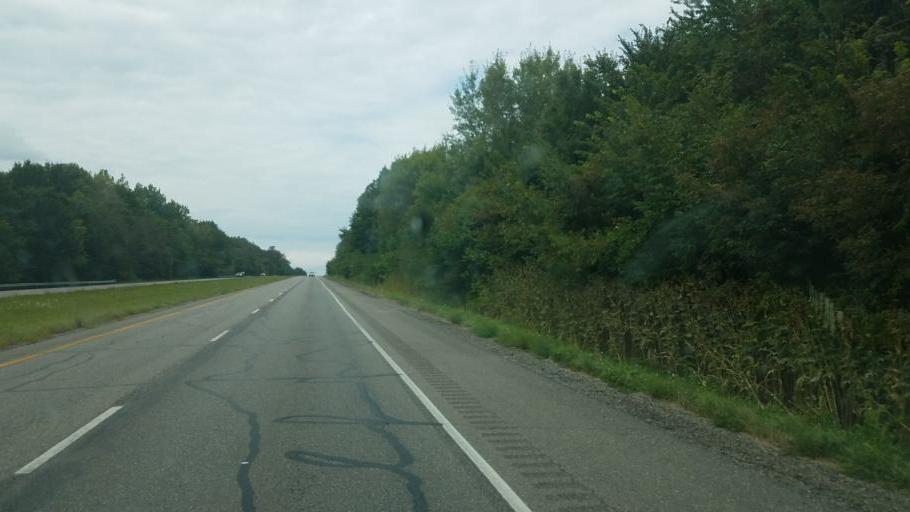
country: US
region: Ohio
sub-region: Columbiana County
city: Lisbon
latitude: 40.7888
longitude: -80.7405
